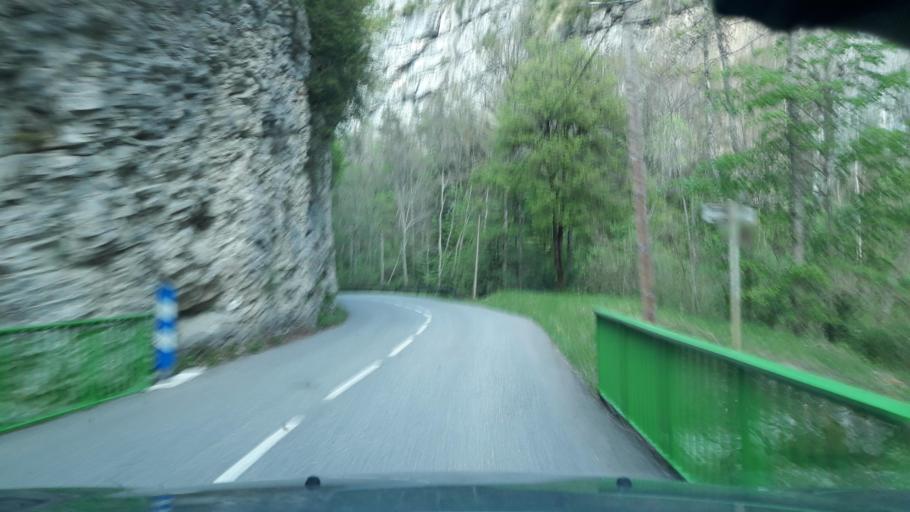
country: FR
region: Rhone-Alpes
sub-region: Departement de la Drome
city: Die
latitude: 44.6830
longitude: 5.5731
